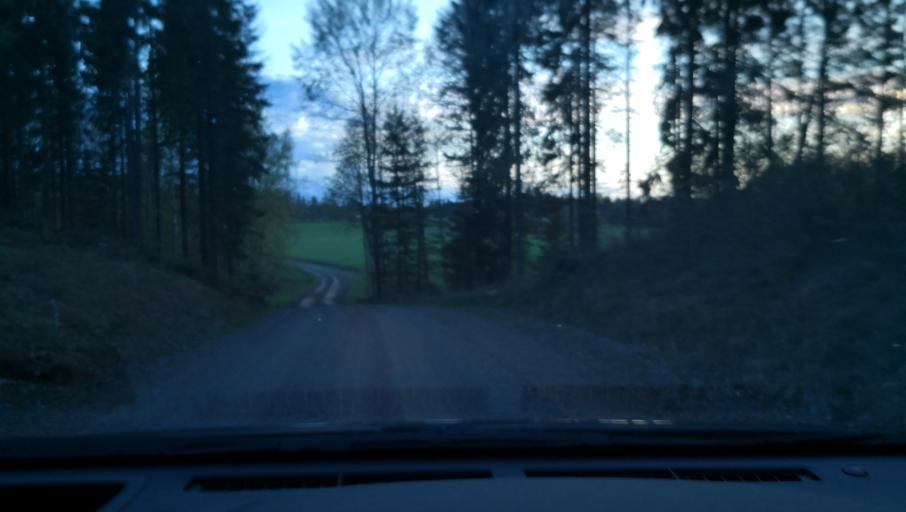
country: SE
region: OErebro
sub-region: Askersunds Kommun
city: Askersund
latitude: 58.9907
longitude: 14.9149
